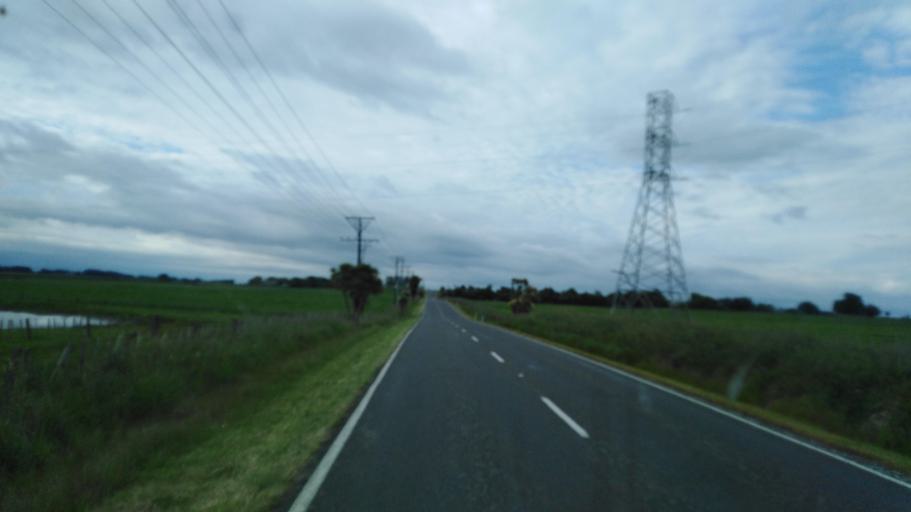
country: NZ
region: Manawatu-Wanganui
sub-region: Rangitikei District
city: Bulls
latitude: -40.1047
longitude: 175.3609
